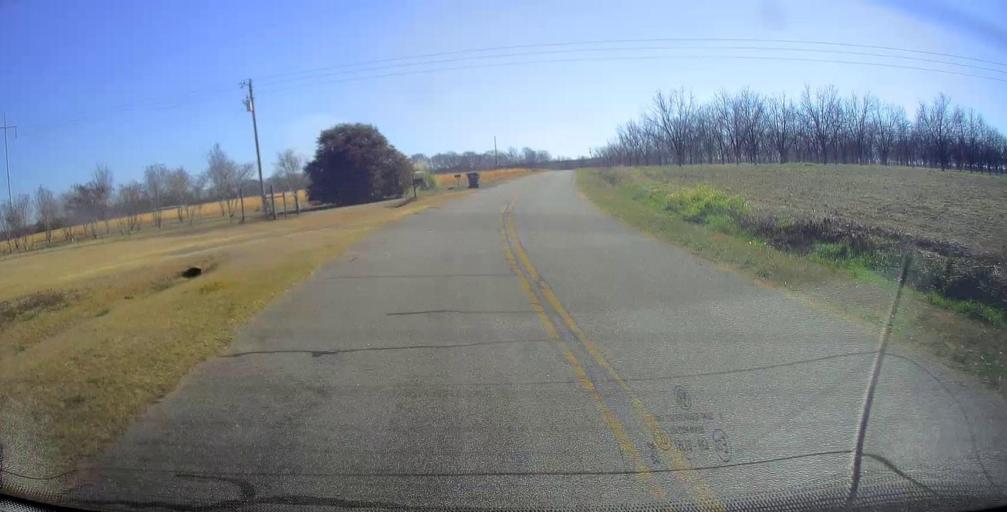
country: US
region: Georgia
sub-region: Peach County
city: Byron
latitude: 32.6280
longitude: -83.8394
